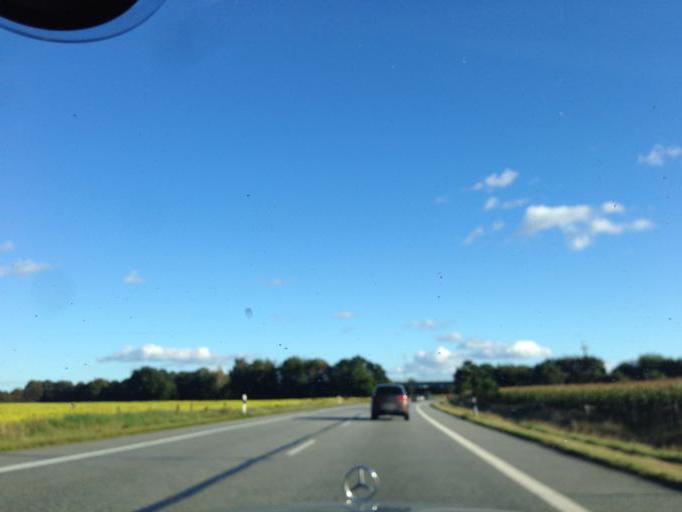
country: DE
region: Schleswig-Holstein
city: Rickling
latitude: 54.0123
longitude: 10.1716
